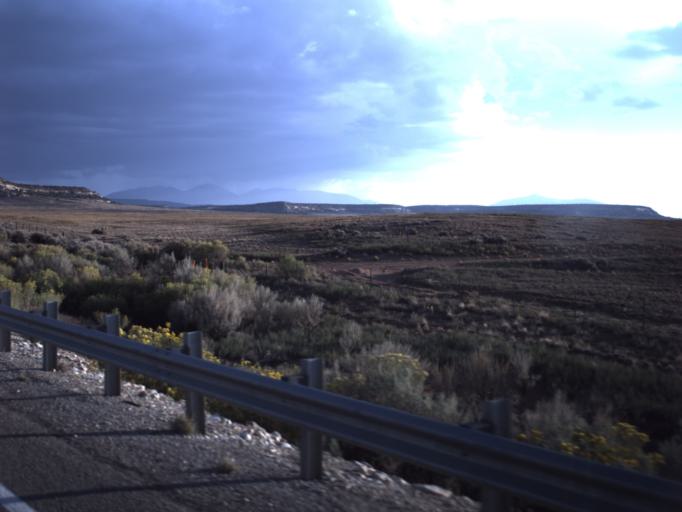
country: US
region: Utah
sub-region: San Juan County
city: Monticello
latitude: 38.1165
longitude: -109.3656
